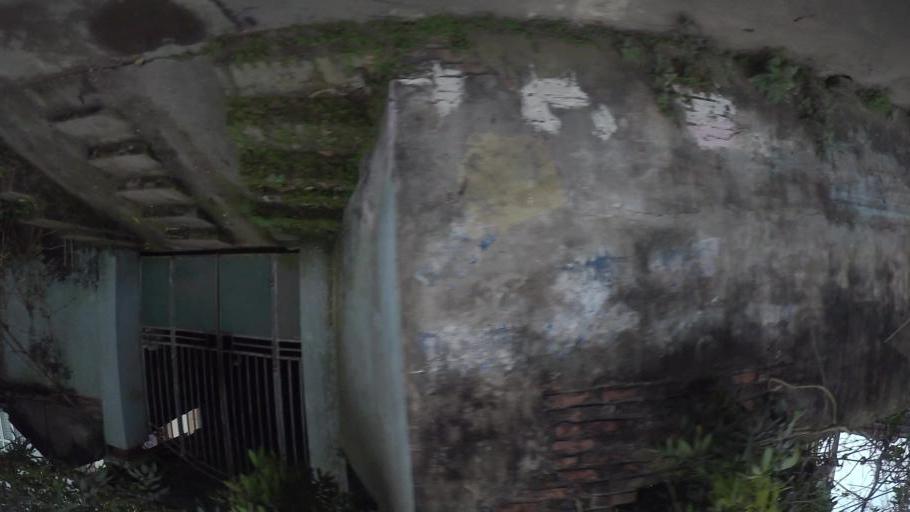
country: VN
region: Ha Noi
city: Trau Quy
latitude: 21.0529
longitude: 105.9230
